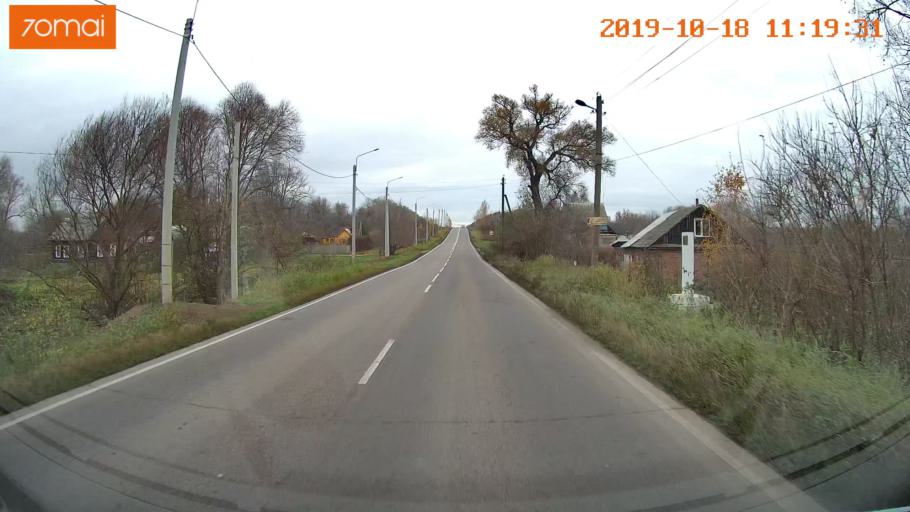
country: RU
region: Tula
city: Kimovsk
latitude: 54.0473
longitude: 38.5543
